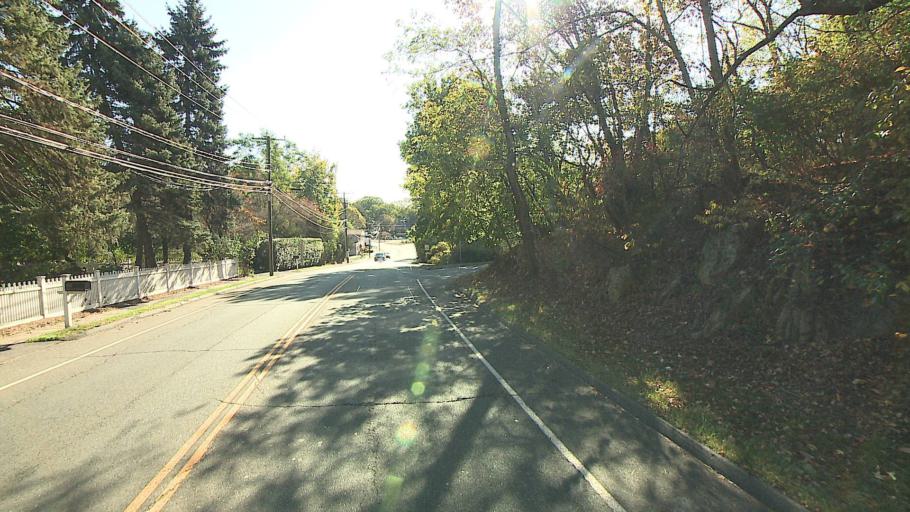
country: US
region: Connecticut
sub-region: Fairfield County
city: Darien
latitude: 41.0741
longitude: -73.4502
